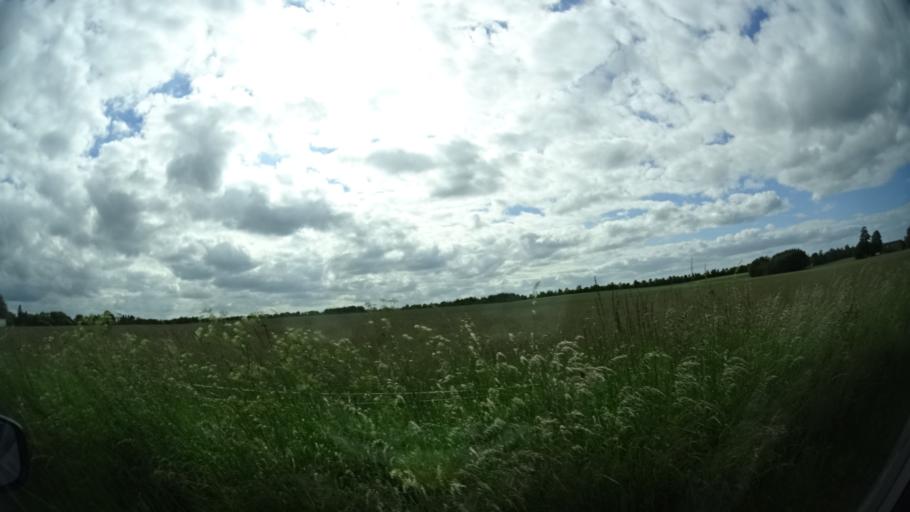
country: DK
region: Central Jutland
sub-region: Norddjurs Kommune
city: Grenaa
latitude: 56.4487
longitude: 10.7113
